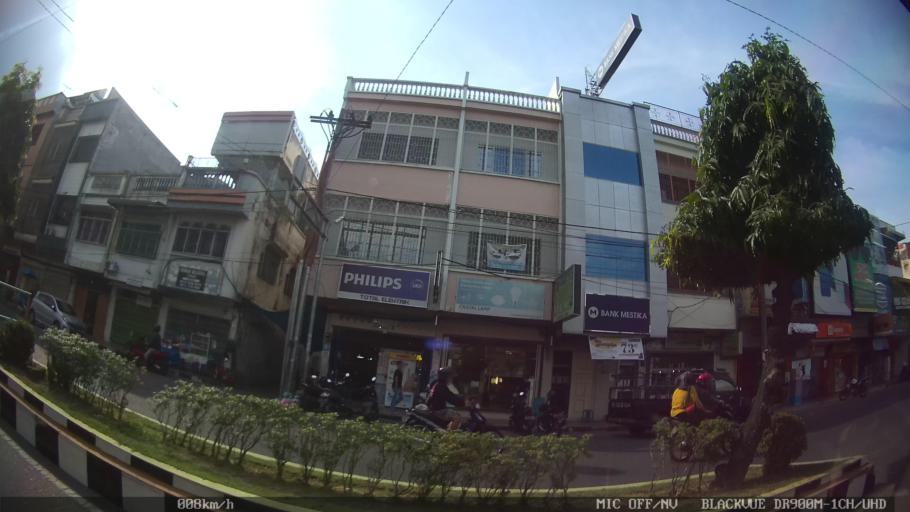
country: ID
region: North Sumatra
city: Binjai
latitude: 3.6054
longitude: 98.4858
